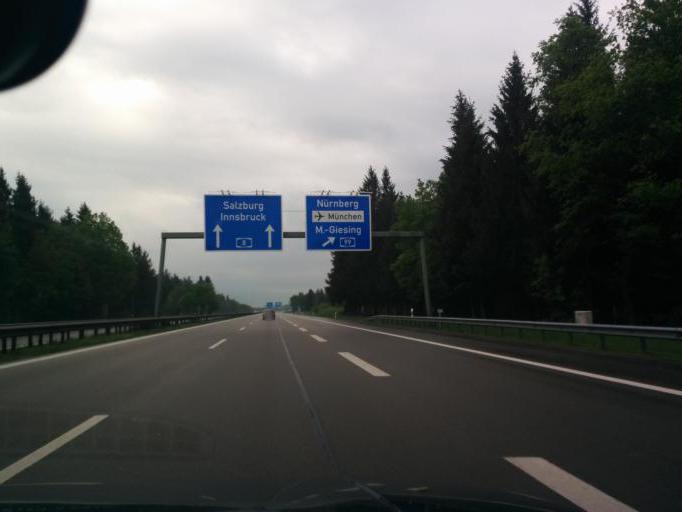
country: DE
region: Bavaria
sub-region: Upper Bavaria
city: Ottobrunn
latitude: 48.0375
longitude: 11.6523
